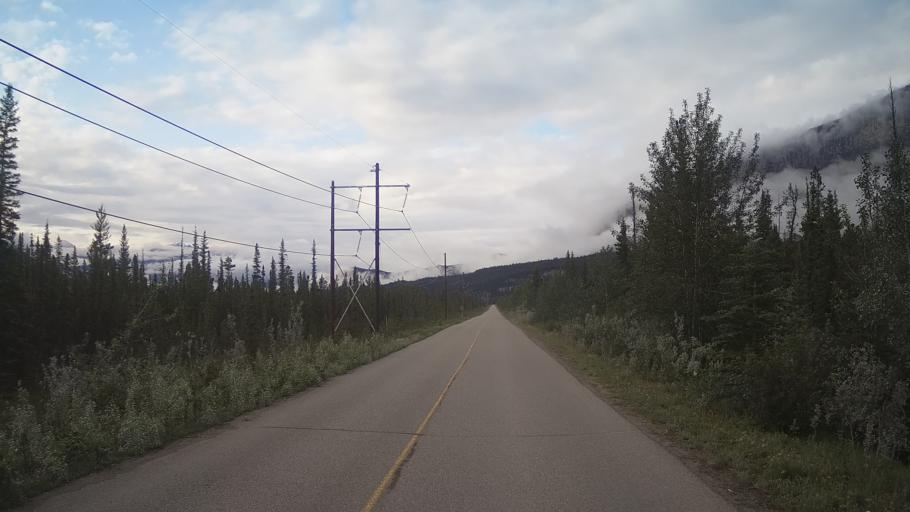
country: CA
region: Alberta
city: Jasper Park Lodge
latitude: 53.0081
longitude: -118.0861
